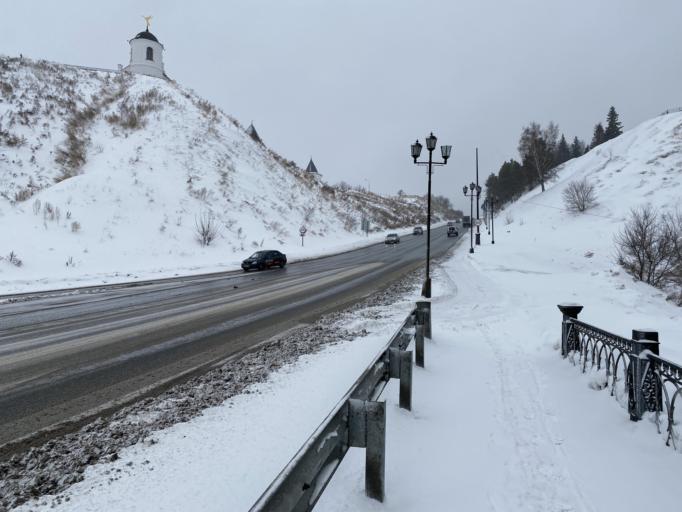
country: RU
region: Tjumen
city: Tobol'sk
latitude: 58.1967
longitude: 68.2553
